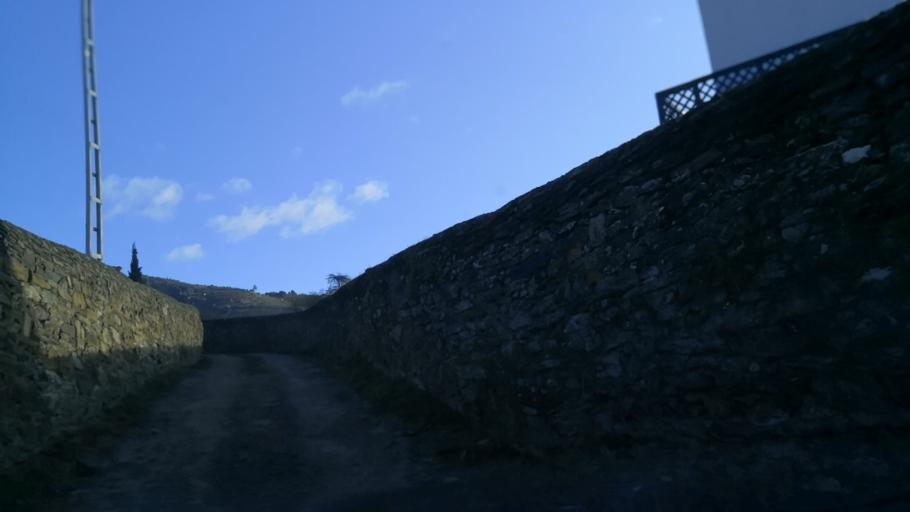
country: PT
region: Vila Real
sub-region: Sabrosa
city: Vilela
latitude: 41.1894
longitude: -7.5403
